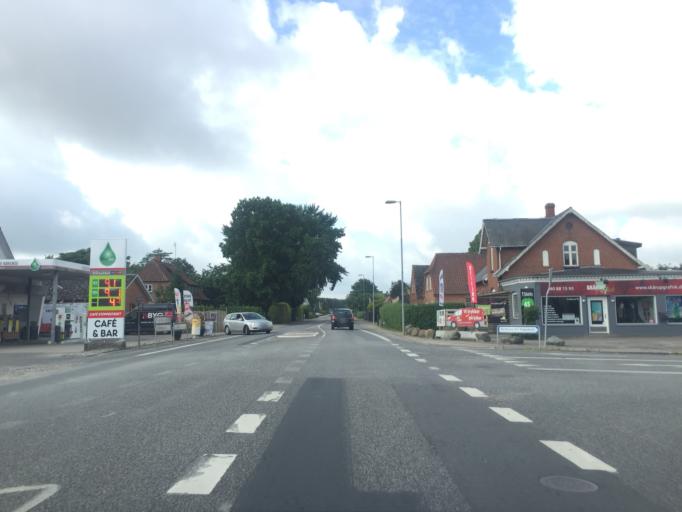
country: DK
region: South Denmark
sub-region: Svendborg Kommune
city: Thuro By
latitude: 55.0897
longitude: 10.6931
